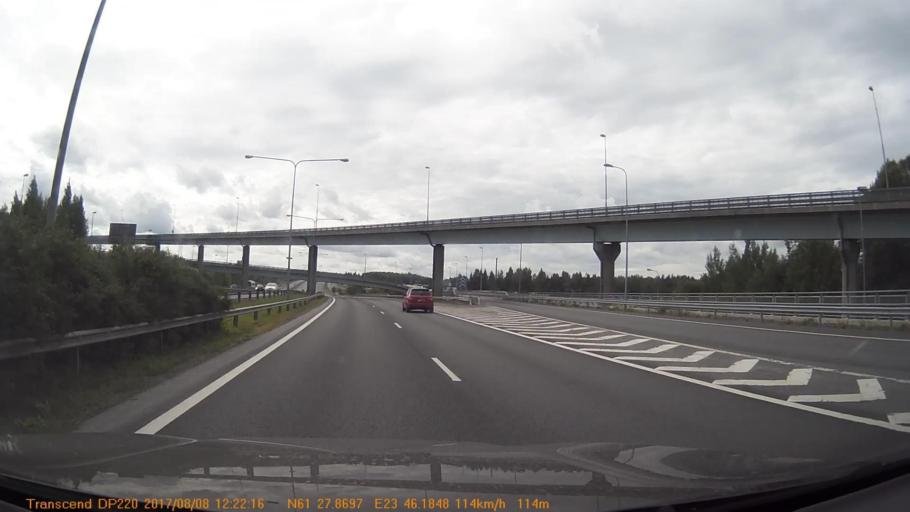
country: FI
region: Pirkanmaa
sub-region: Tampere
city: Tampere
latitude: 61.4641
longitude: 23.7697
